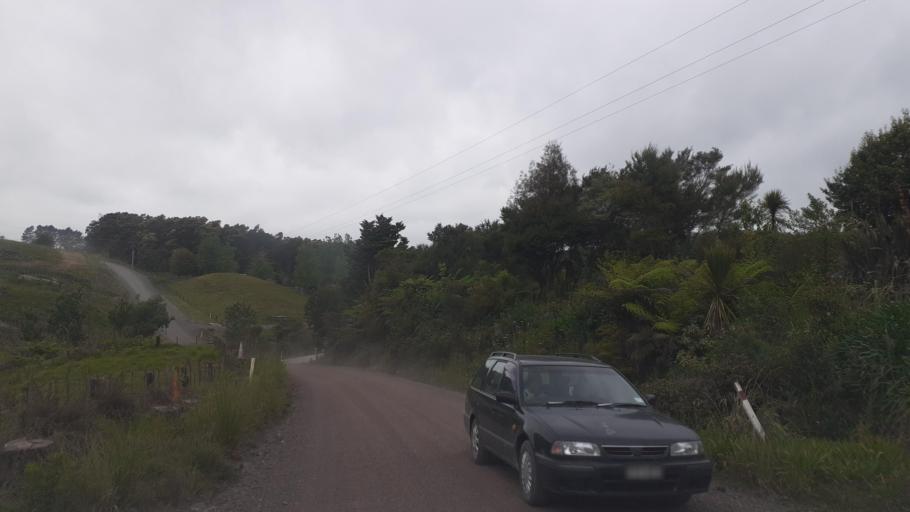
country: NZ
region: Northland
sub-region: Far North District
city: Kerikeri
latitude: -35.2799
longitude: 173.9650
